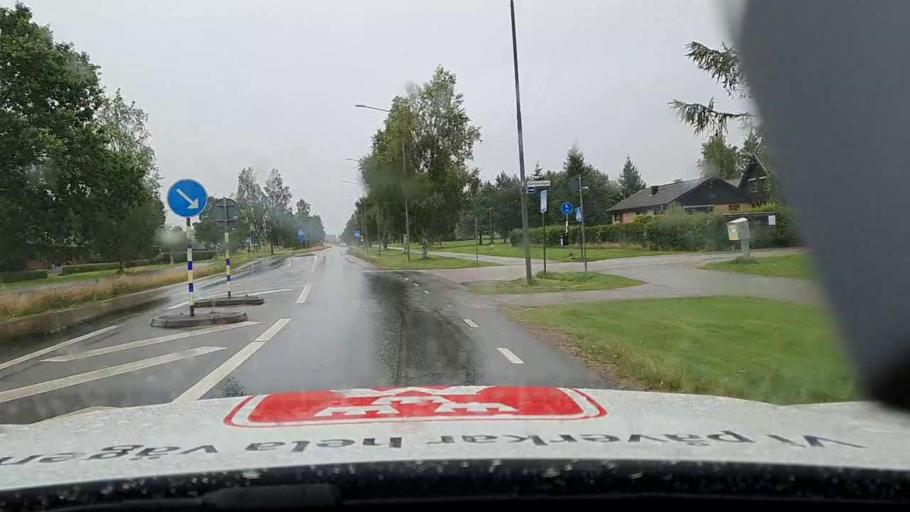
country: SE
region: Vaestra Goetaland
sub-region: Toreboda Kommun
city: Toereboda
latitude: 58.7052
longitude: 14.1352
